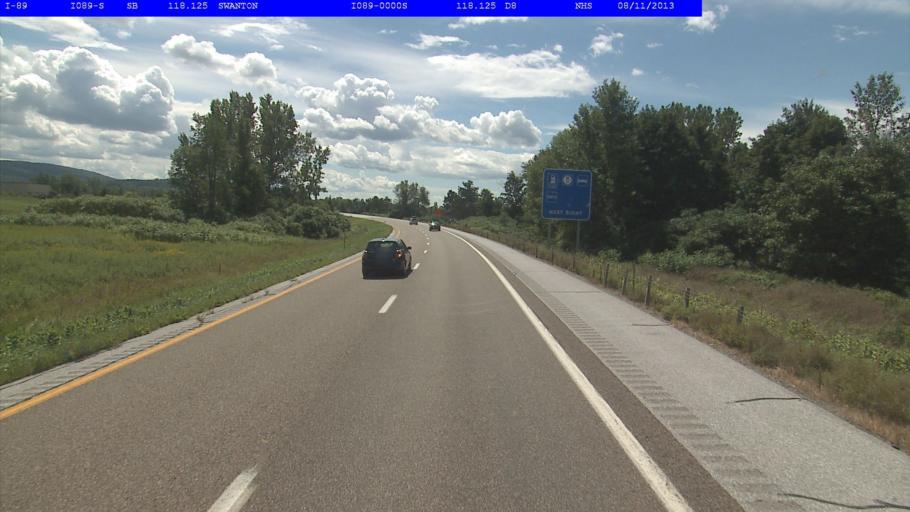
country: US
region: Vermont
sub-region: Franklin County
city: Saint Albans
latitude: 44.8502
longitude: -73.0835
